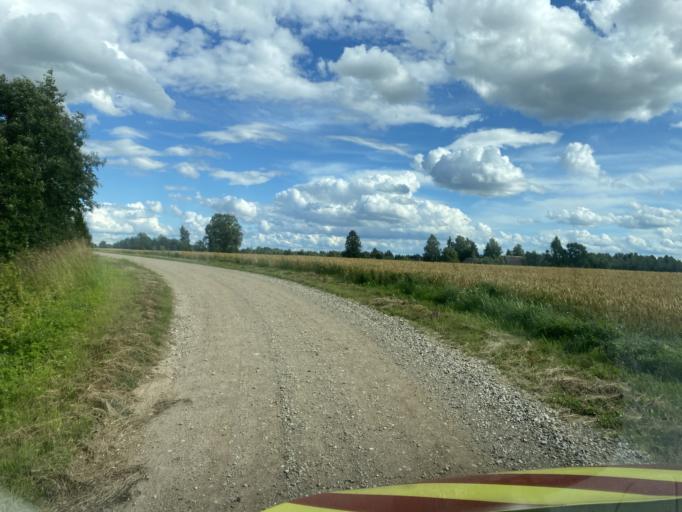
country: EE
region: Viljandimaa
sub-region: Viiratsi vald
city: Viiratsi
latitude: 58.4000
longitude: 25.8051
